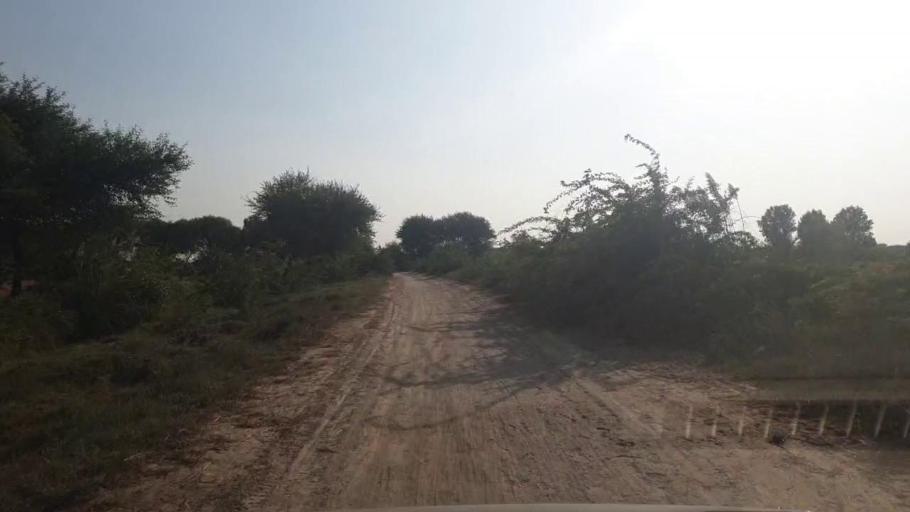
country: PK
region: Sindh
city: Badin
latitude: 24.6382
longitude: 68.7994
